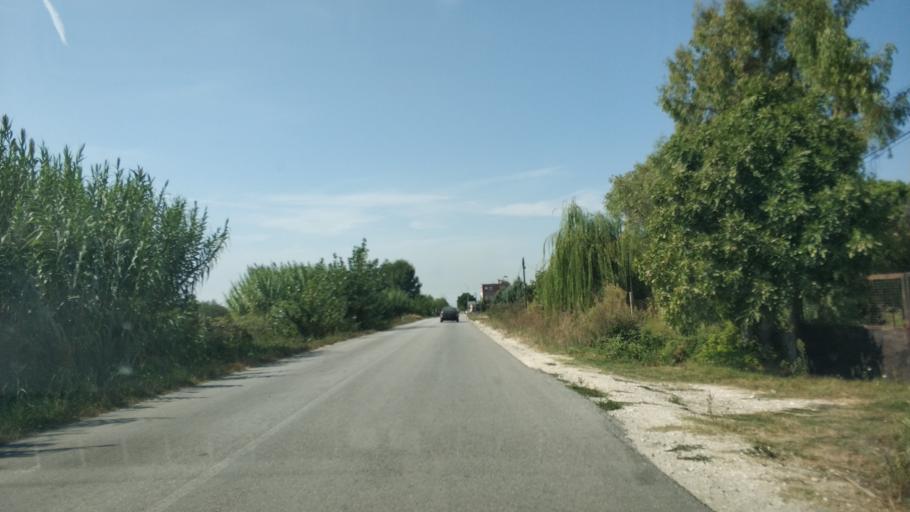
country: AL
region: Fier
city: Fier
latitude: 40.7349
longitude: 19.5266
